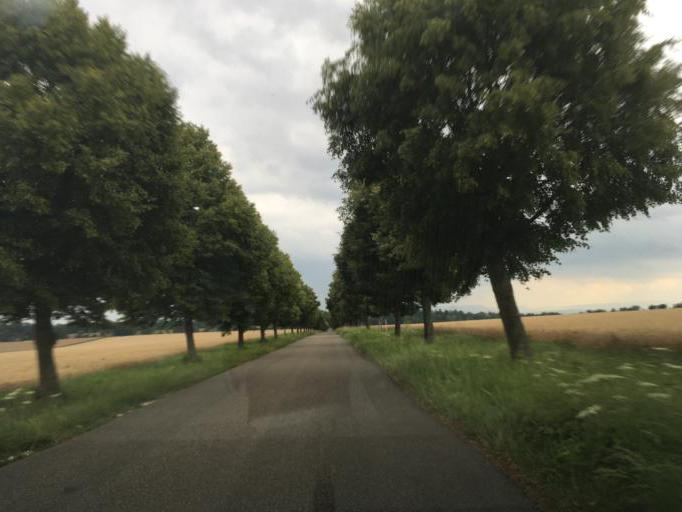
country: DE
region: Baden-Wuerttemberg
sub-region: Tuebingen Region
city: Kirchentellinsfurt
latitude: 48.5531
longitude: 9.1326
